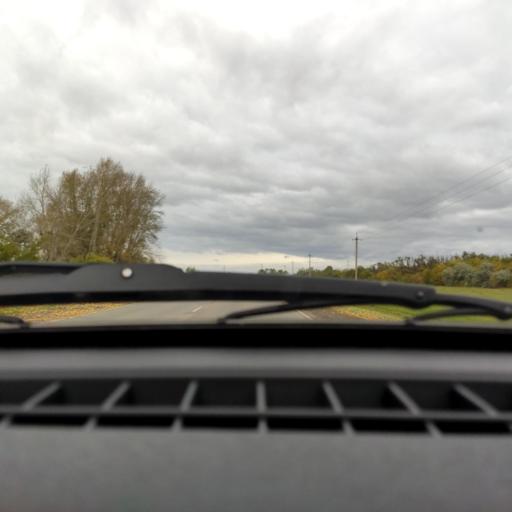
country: RU
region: Bashkortostan
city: Rayevskiy
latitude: 54.0329
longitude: 54.9058
